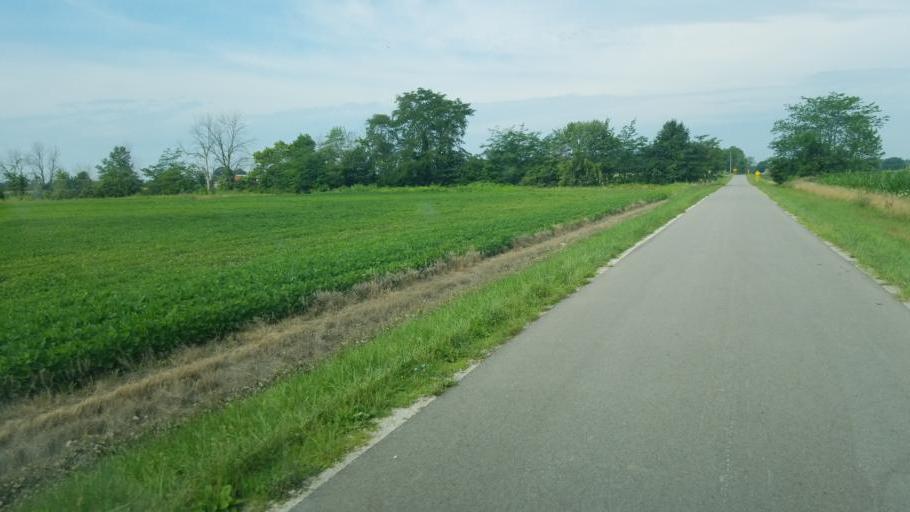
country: US
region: Ohio
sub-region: Wyandot County
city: Upper Sandusky
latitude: 40.6727
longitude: -83.3130
